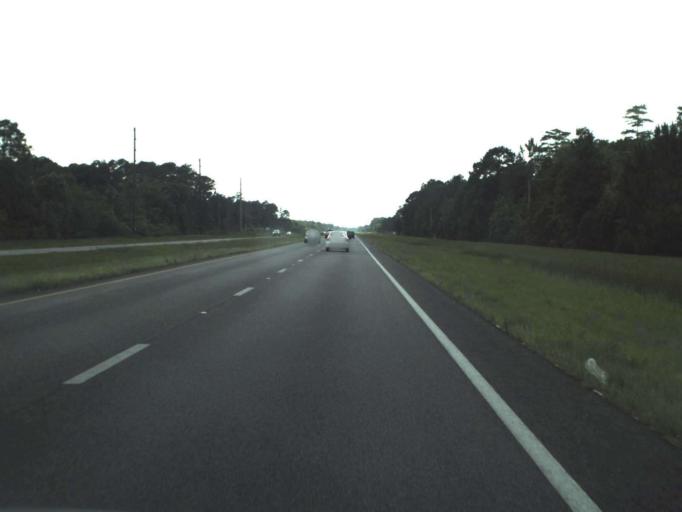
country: US
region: Florida
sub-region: Volusia County
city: Samsula-Spruce Creek
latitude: 29.0119
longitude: -81.0373
